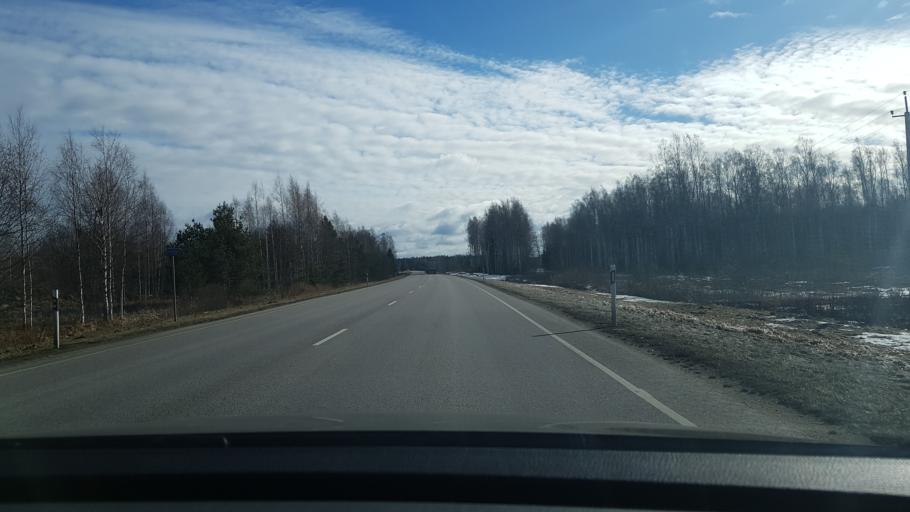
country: EE
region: Paernumaa
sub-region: Saarde vald
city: Kilingi-Nomme
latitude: 58.1750
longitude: 24.8059
